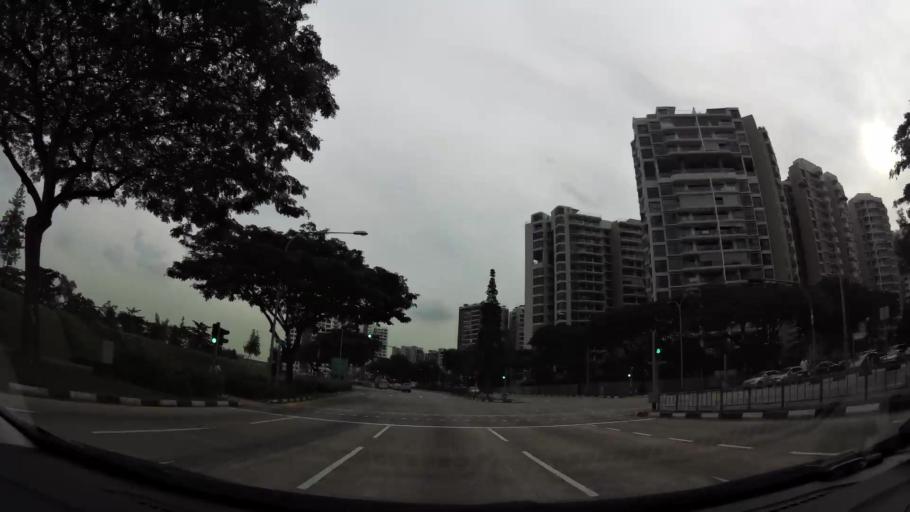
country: MY
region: Johor
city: Kampung Pasir Gudang Baru
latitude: 1.3820
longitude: 103.9035
